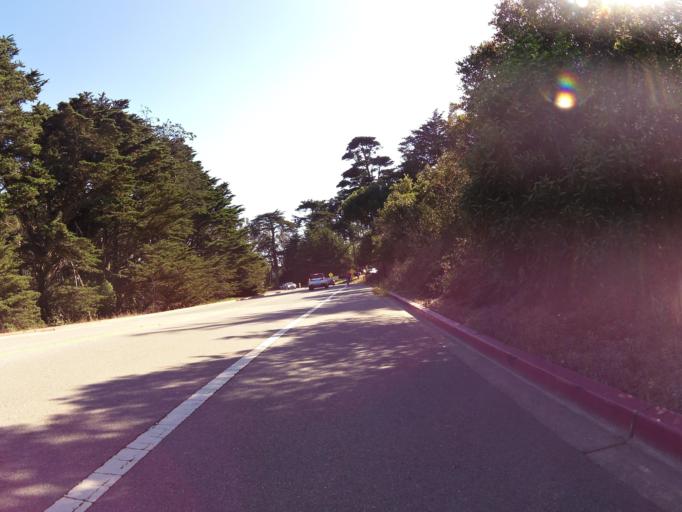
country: US
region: California
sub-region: San Francisco County
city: San Francisco
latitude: 37.7917
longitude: -122.4588
